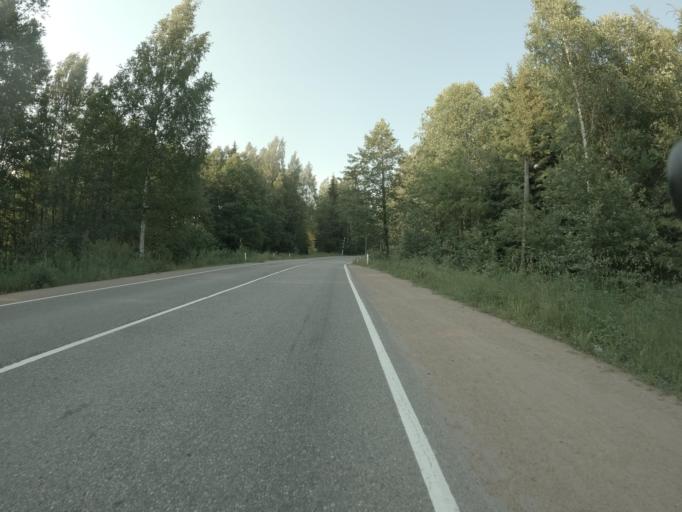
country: RU
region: Leningrad
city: Veshchevo
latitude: 60.4716
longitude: 29.2578
